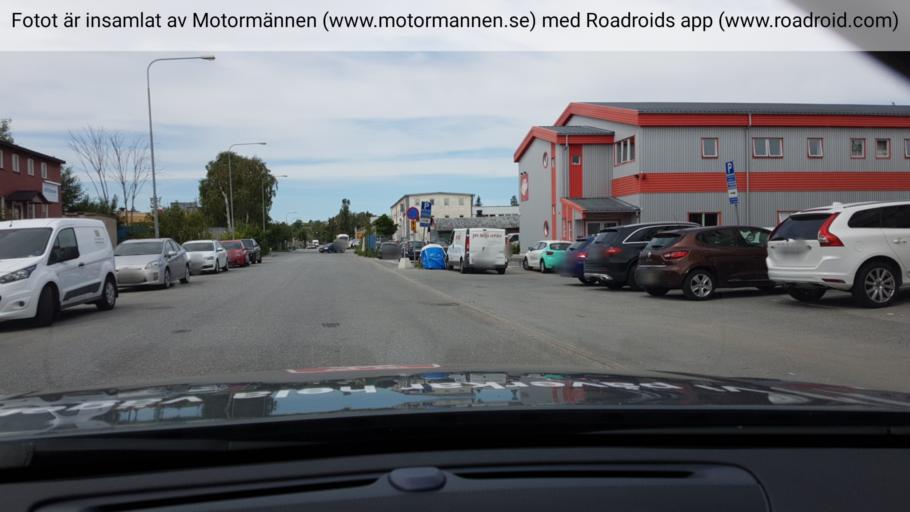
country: SE
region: Stockholm
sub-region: Huddinge Kommun
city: Huddinge
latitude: 59.2305
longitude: 17.9913
